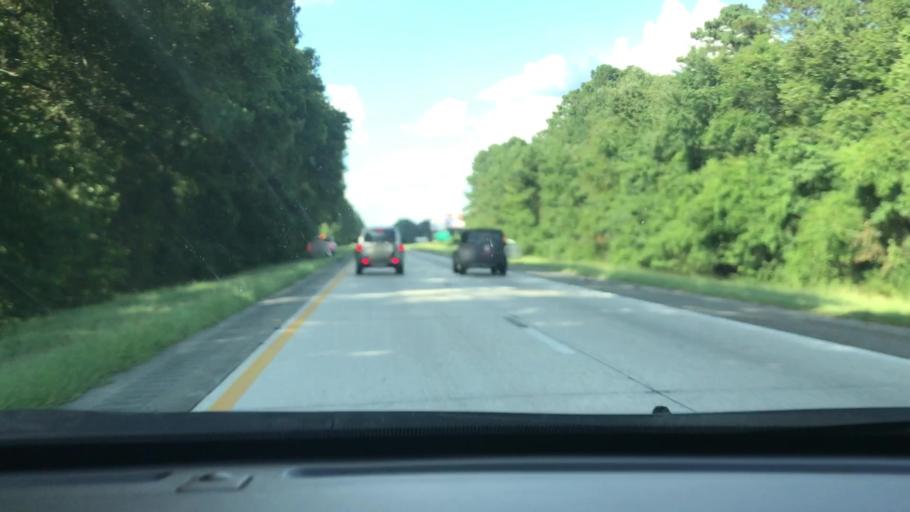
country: US
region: South Carolina
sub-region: Florence County
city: Timmonsville
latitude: 34.0995
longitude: -79.9240
